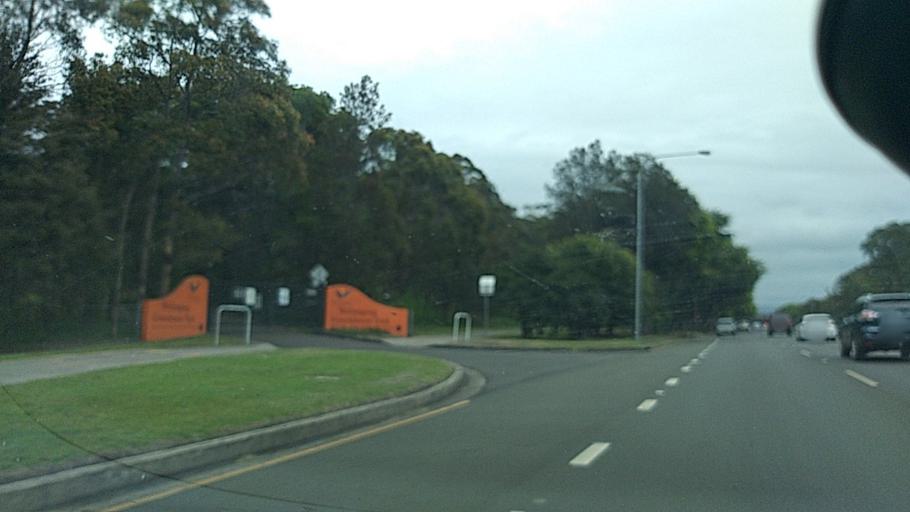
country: AU
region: New South Wales
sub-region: Wollongong
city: Coniston
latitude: -34.4394
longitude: 150.8938
